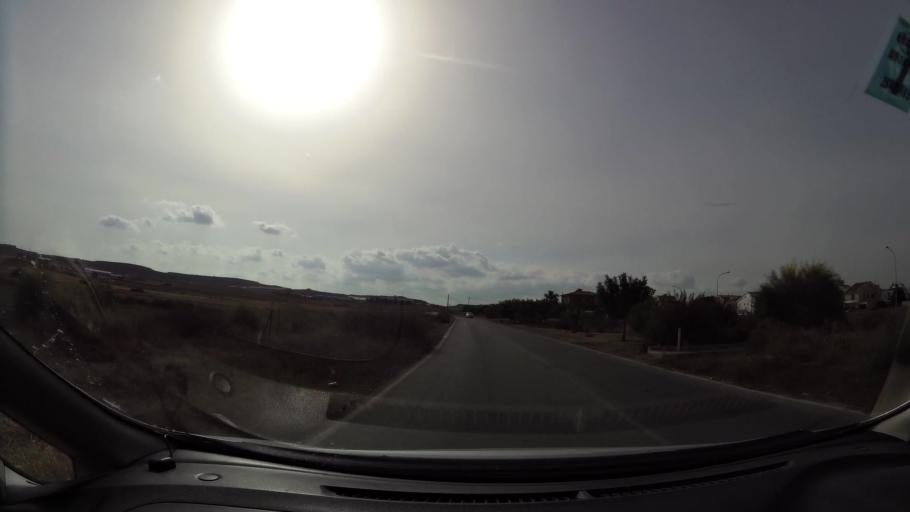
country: CY
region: Lefkosia
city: Geri
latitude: 35.0780
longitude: 33.3983
